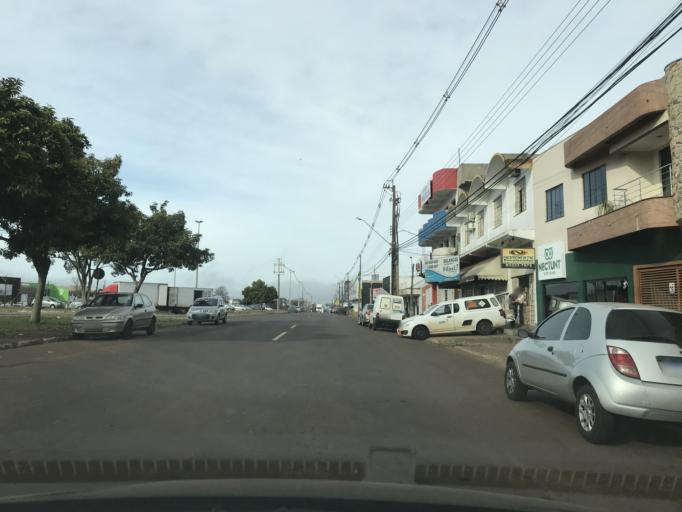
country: BR
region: Parana
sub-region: Cascavel
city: Cascavel
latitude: -24.9580
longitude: -53.4808
